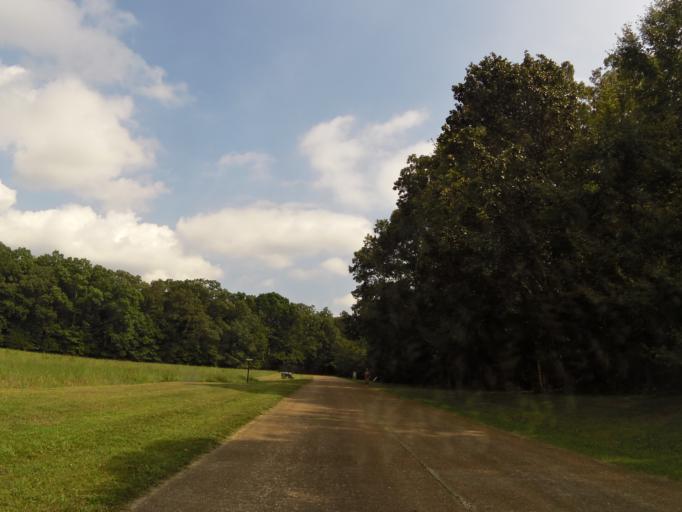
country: US
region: Tennessee
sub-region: Hardin County
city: Crump
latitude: 35.1306
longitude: -88.3392
